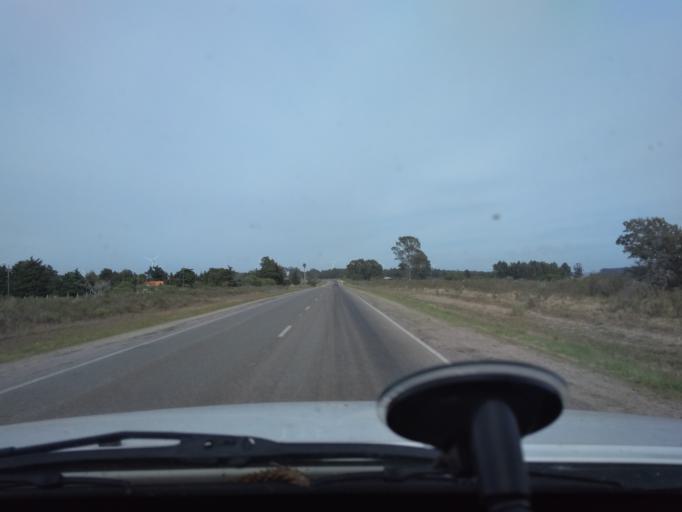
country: UY
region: Florida
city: Florida
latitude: -34.0740
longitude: -56.0745
